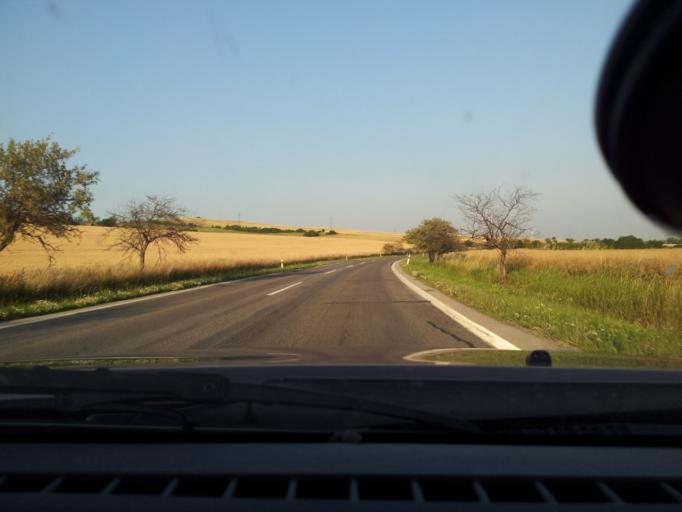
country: SK
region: Trnavsky
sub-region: Okres Skalica
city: Skalica
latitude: 48.7847
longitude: 17.2269
